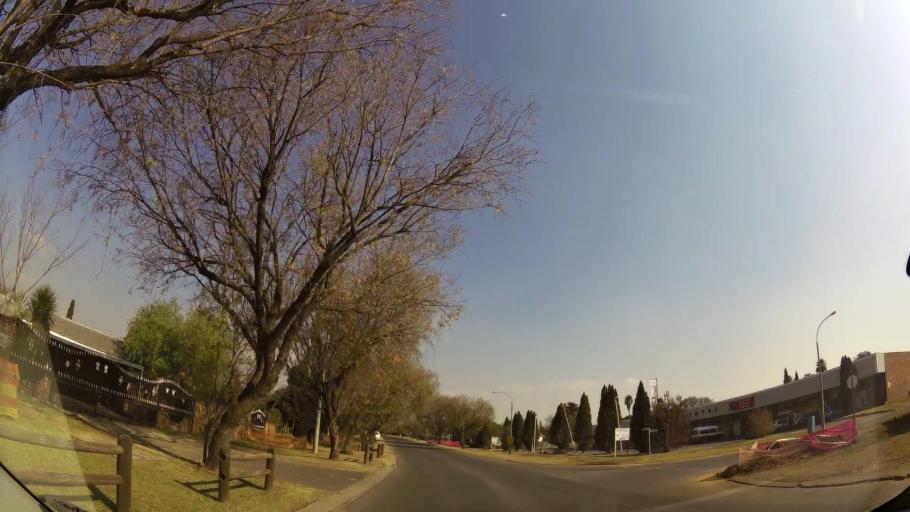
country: ZA
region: Gauteng
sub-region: Ekurhuleni Metropolitan Municipality
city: Benoni
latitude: -26.1473
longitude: 28.2852
